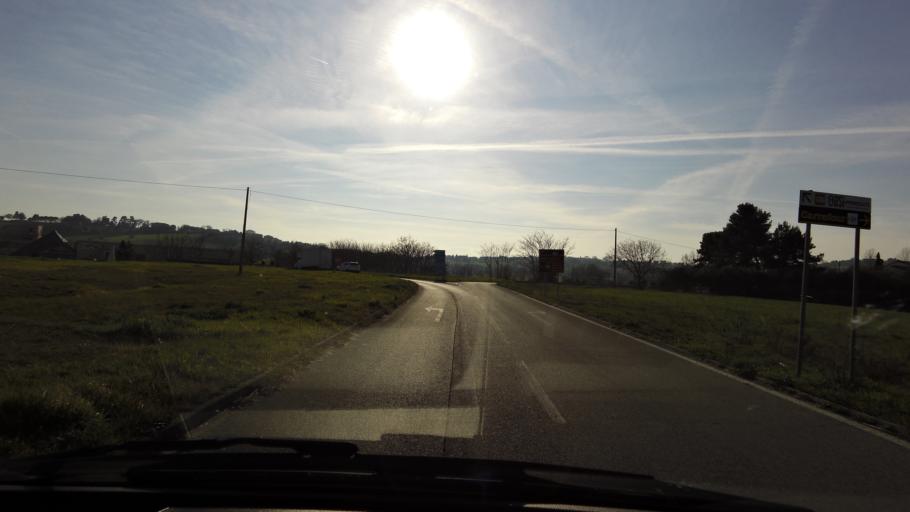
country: IT
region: The Marches
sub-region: Provincia di Ancona
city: Villa Musone
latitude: 43.4765
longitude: 13.5829
